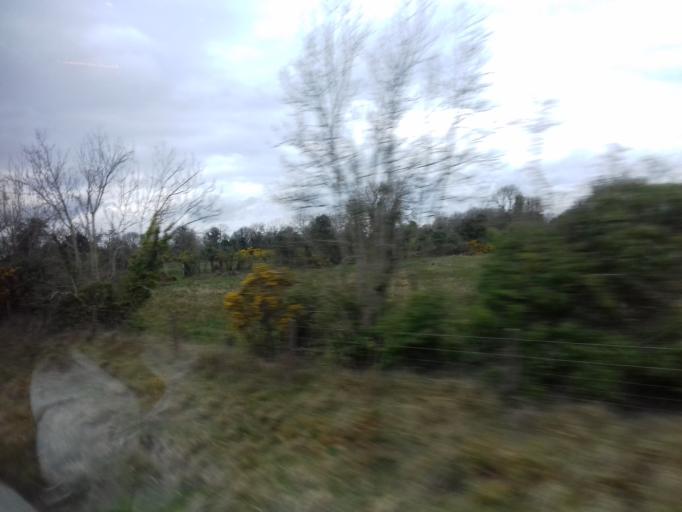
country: IE
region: Leinster
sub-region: An Longfort
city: Edgeworthstown
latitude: 53.6971
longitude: -7.6476
